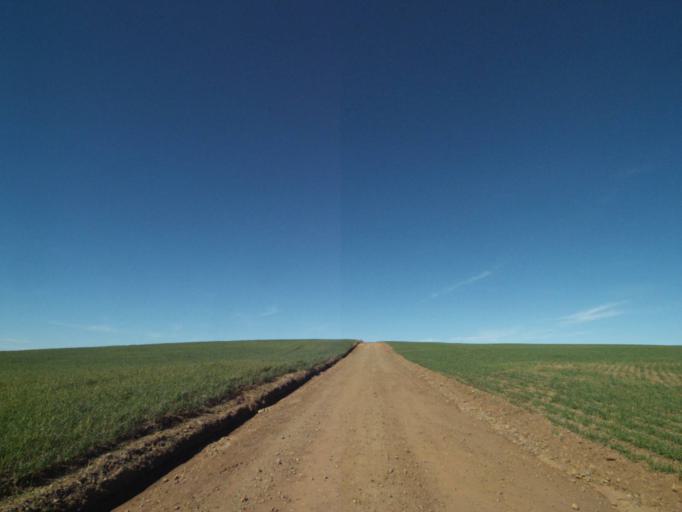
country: BR
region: Parana
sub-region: Tibagi
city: Tibagi
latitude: -24.5716
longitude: -50.2661
